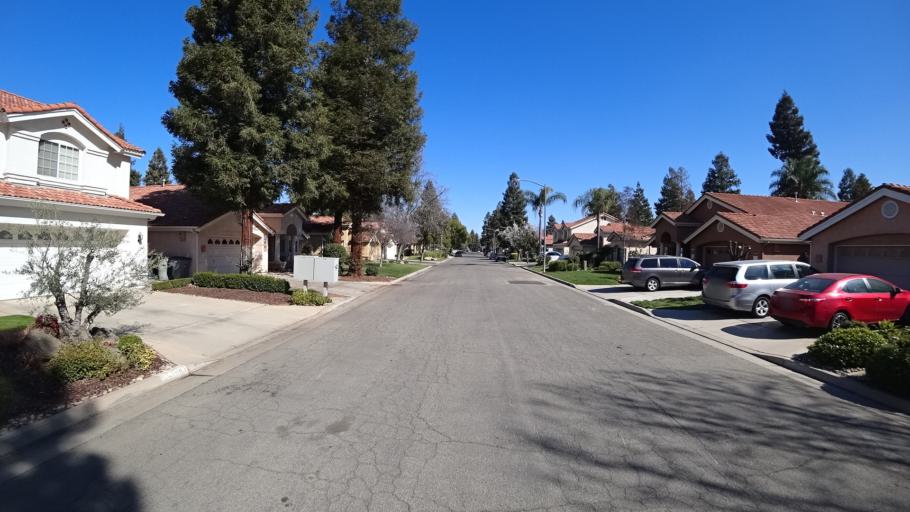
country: US
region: California
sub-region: Fresno County
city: Clovis
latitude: 36.8642
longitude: -119.7511
